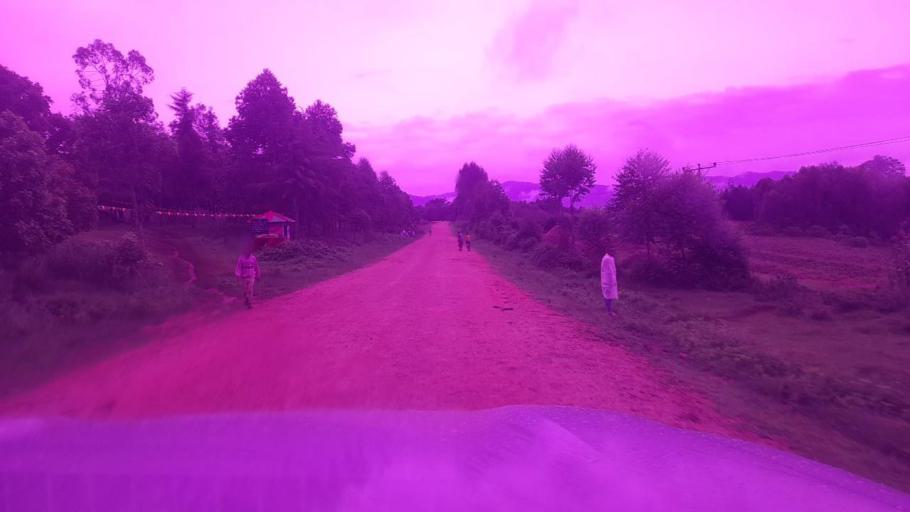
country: ET
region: Southern Nations, Nationalities, and People's Region
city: Bonga
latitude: 7.4409
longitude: 36.1597
